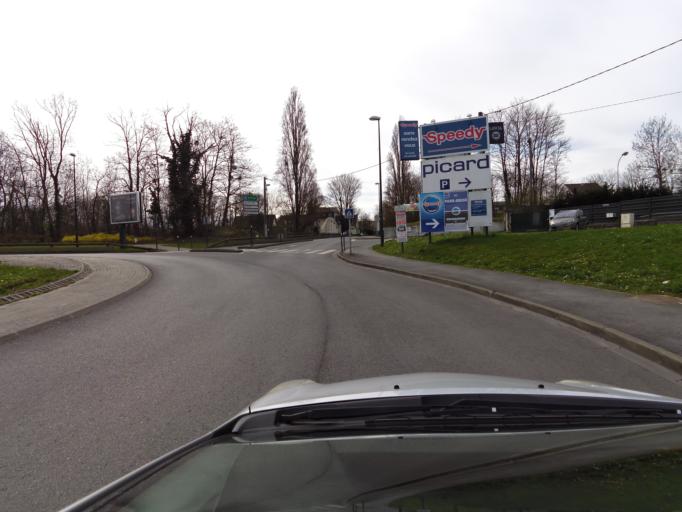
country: FR
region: Ile-de-France
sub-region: Departement de Seine-et-Marne
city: Villeparisis
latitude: 48.9527
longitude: 2.6060
